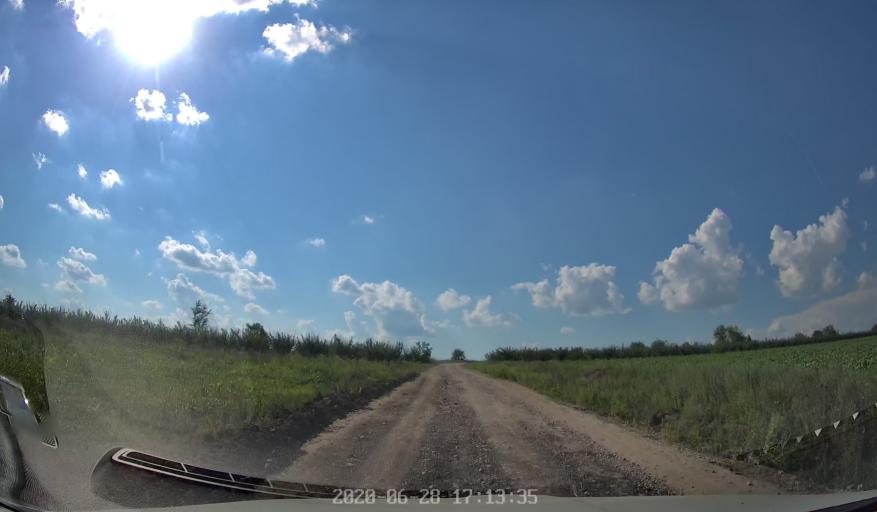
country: MD
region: Chisinau
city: Vatra
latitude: 46.9910
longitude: 28.6968
